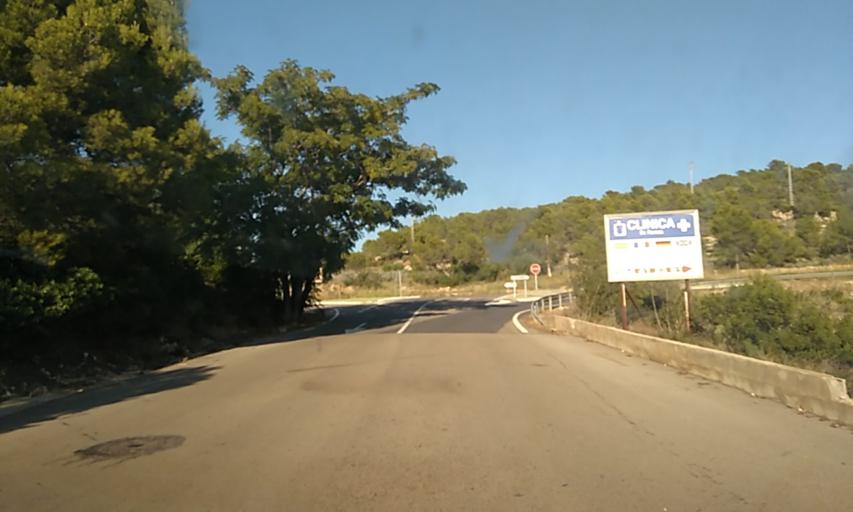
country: ES
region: Valencia
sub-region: Provincia de Castello
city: Alcoceber
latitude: 40.2500
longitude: 0.2470
